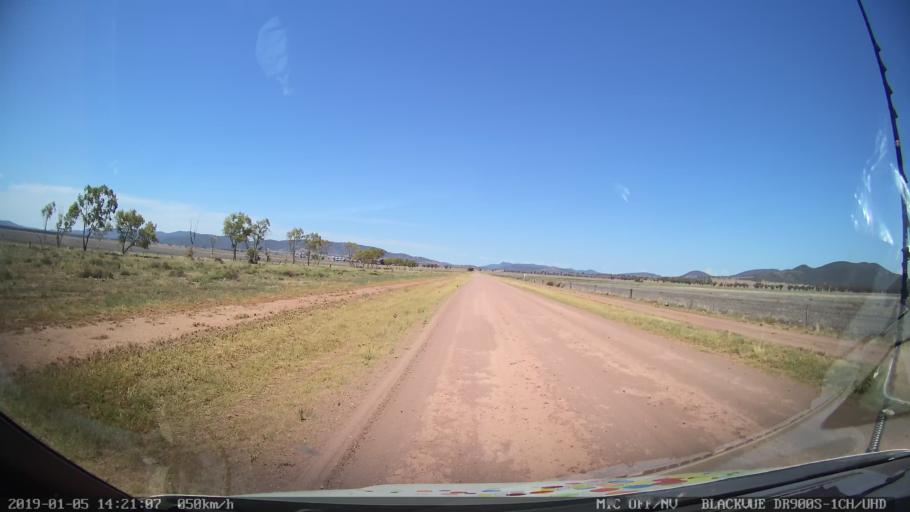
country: AU
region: New South Wales
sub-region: Liverpool Plains
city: Quirindi
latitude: -31.2470
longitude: 150.5108
